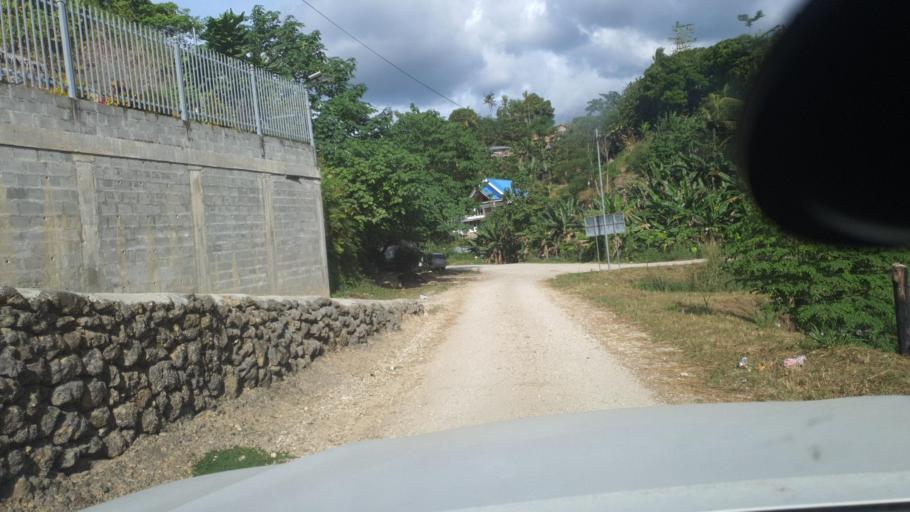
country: SB
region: Guadalcanal
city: Honiara
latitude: -9.4392
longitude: 159.9463
